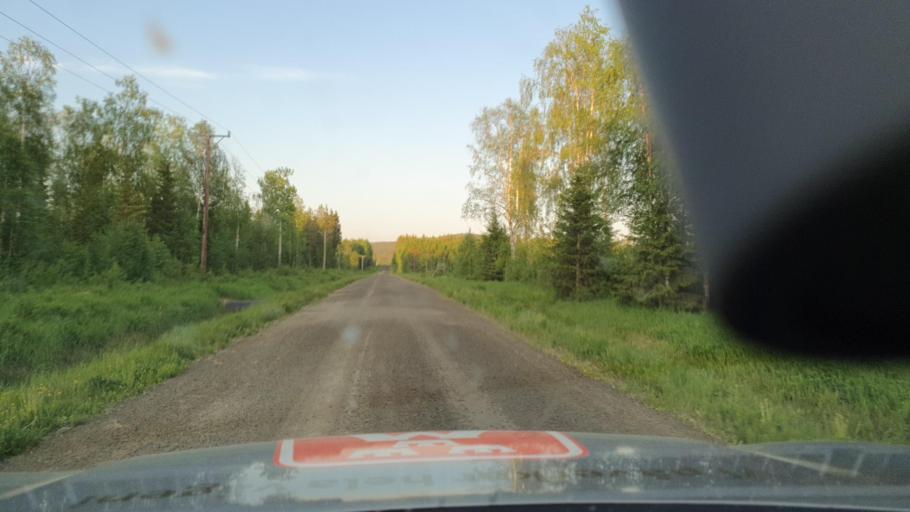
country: SE
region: Norrbotten
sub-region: Bodens Kommun
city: Boden
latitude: 66.0785
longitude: 21.6742
